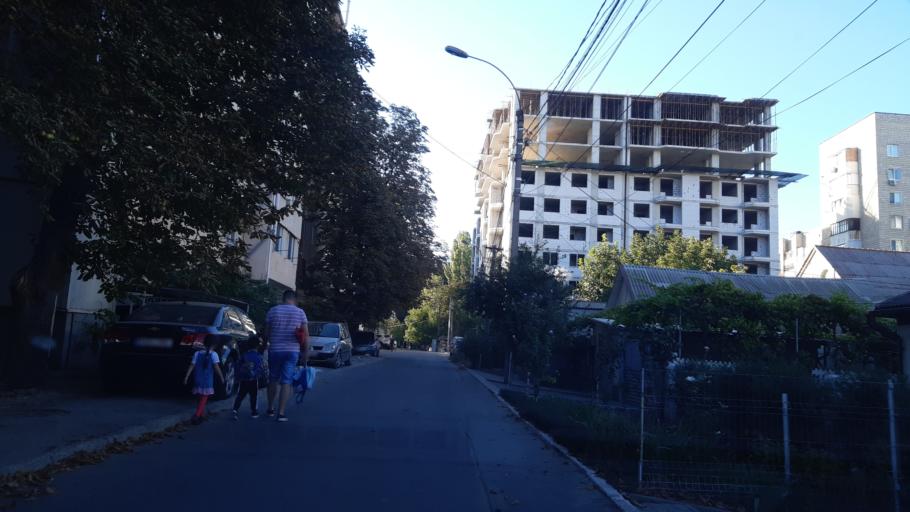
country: MD
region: Chisinau
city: Vatra
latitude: 47.0331
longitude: 28.7776
